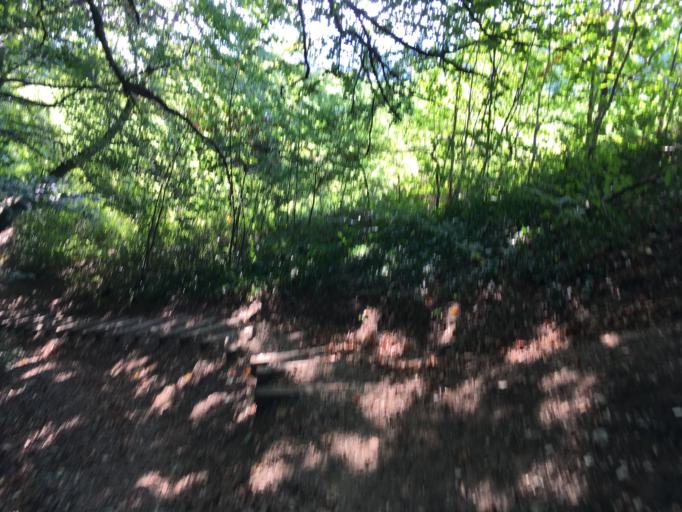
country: CH
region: Zurich
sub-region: Bezirk Hinwil
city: Wetzikon / Kempten
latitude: 47.3389
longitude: 8.8192
